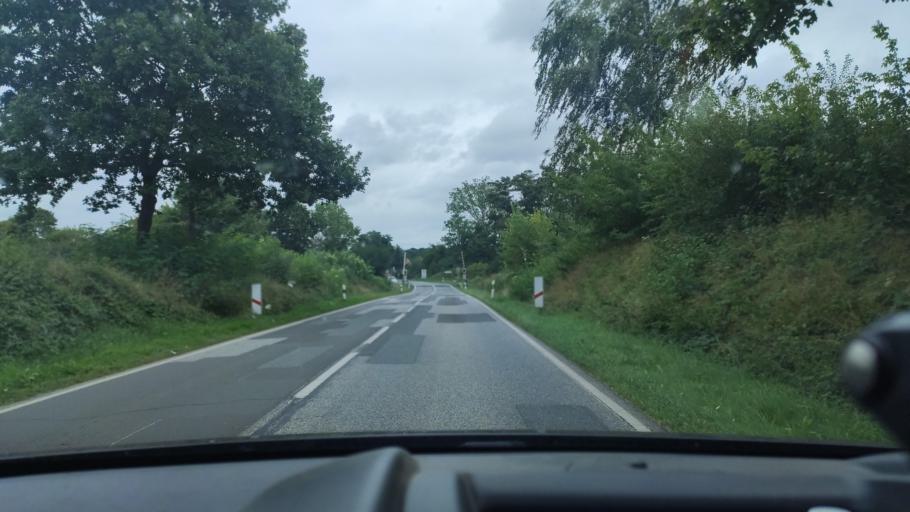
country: DE
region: Mecklenburg-Vorpommern
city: Guestrow
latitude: 53.8386
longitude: 12.1333
